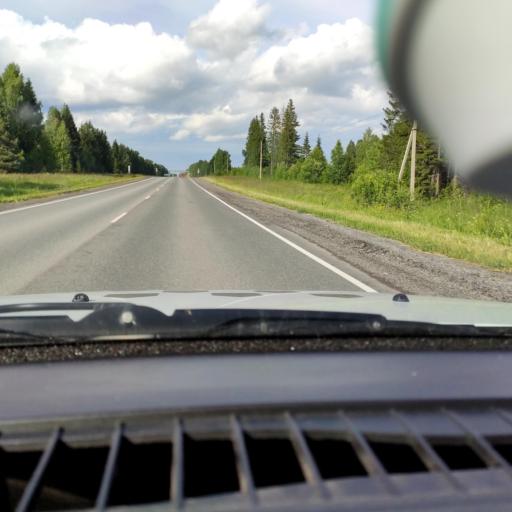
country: RU
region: Perm
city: Orda
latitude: 57.2555
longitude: 57.0049
